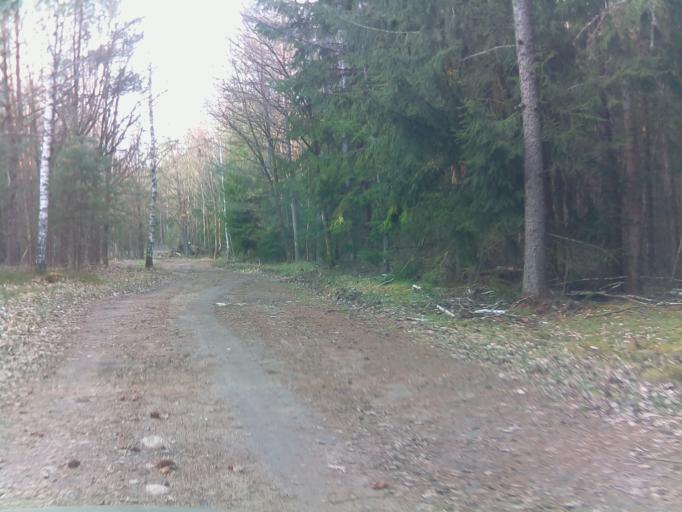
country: DE
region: Brandenburg
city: Schenkendobern
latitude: 51.9989
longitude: 14.5342
